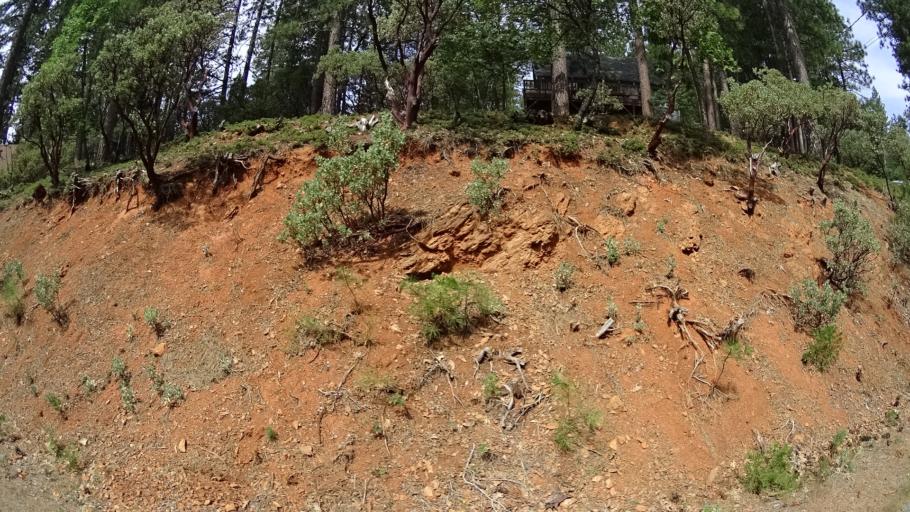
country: US
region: California
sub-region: Calaveras County
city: Arnold
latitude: 38.2424
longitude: -120.3497
